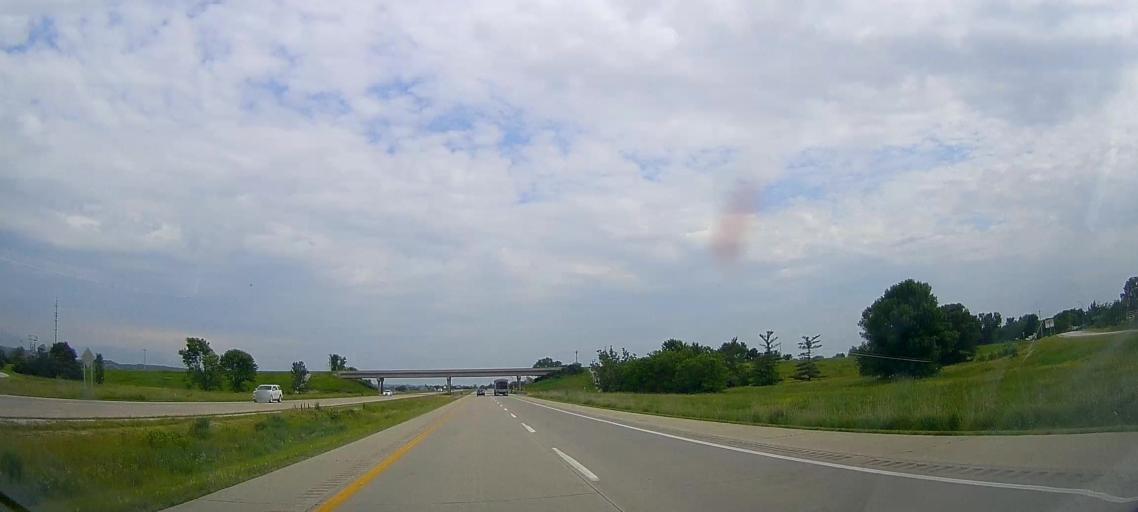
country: US
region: Nebraska
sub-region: Burt County
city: Tekamah
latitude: 41.8032
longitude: -96.0567
